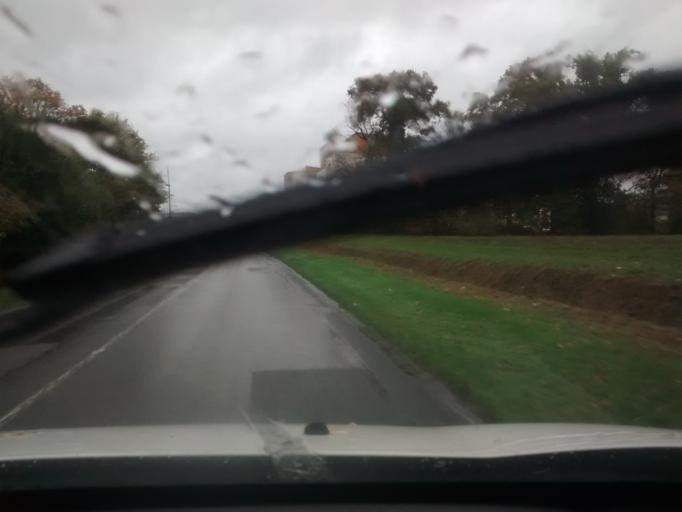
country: FR
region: Brittany
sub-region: Departement d'Ille-et-Vilaine
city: Fouillard
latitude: 48.1475
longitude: -1.5784
